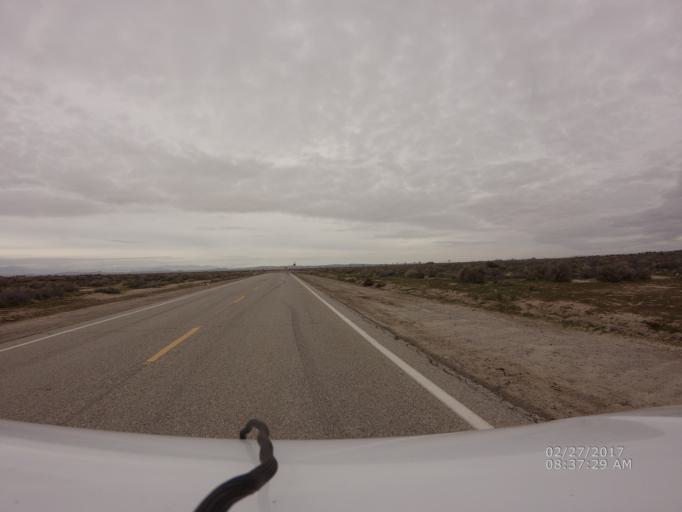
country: US
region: California
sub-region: Los Angeles County
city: Lancaster
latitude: 34.7326
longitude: -118.0590
